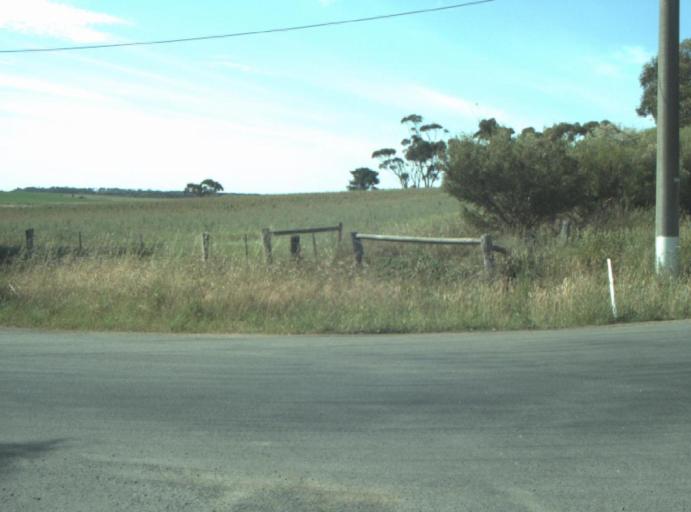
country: AU
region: Victoria
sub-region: Greater Geelong
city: Clifton Springs
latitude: -38.1700
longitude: 144.5151
